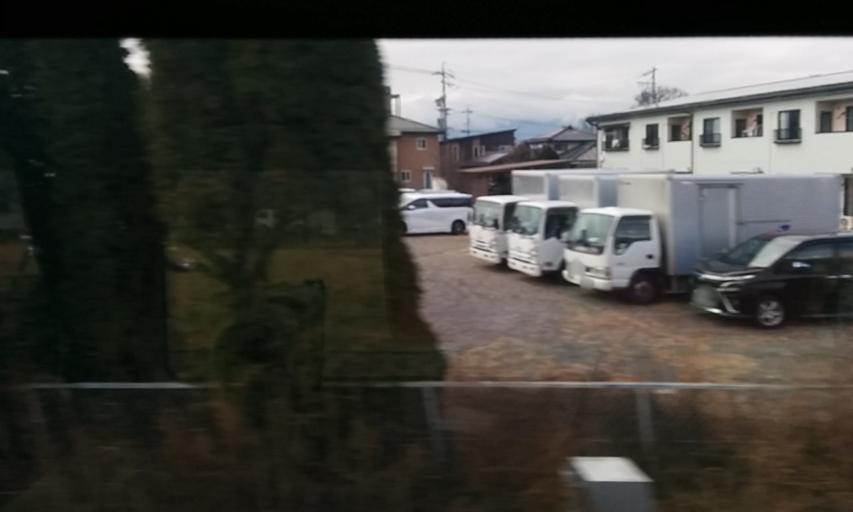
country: JP
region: Nagano
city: Matsumoto
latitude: 36.1947
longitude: 137.9636
